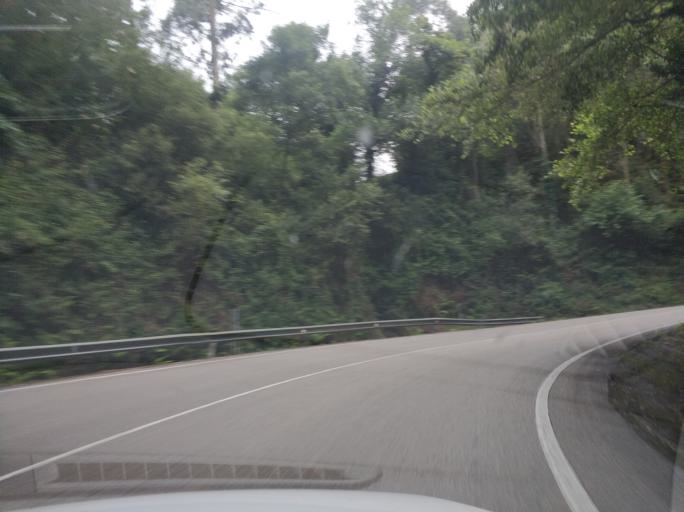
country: ES
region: Asturias
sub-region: Province of Asturias
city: Cudillero
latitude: 43.5640
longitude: -6.1549
